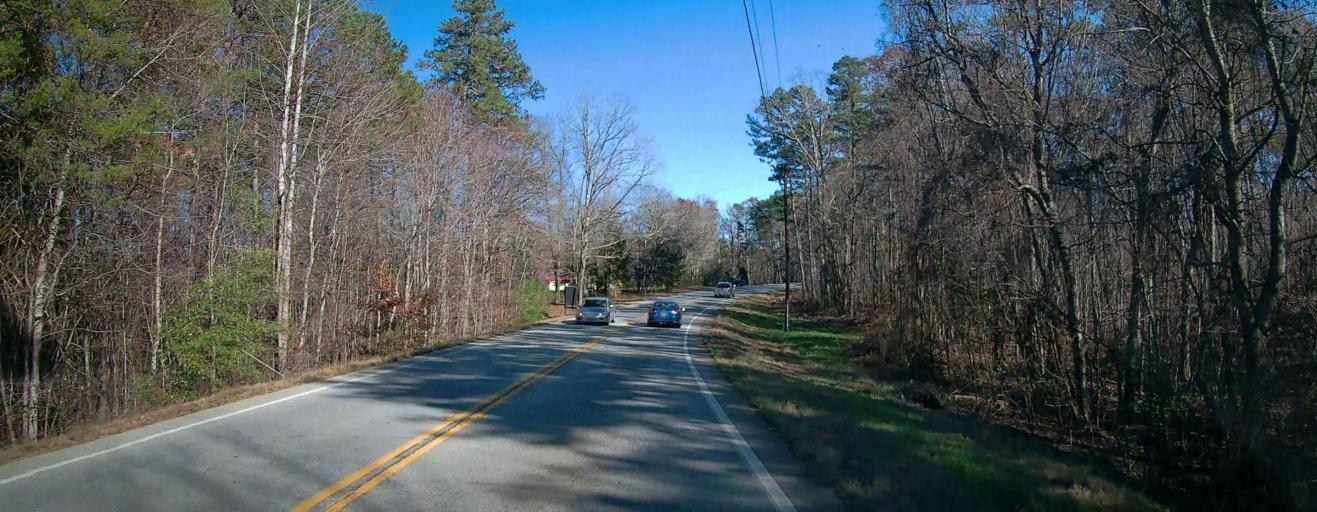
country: US
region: Georgia
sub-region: Hall County
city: Lula
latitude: 34.4061
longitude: -83.7026
